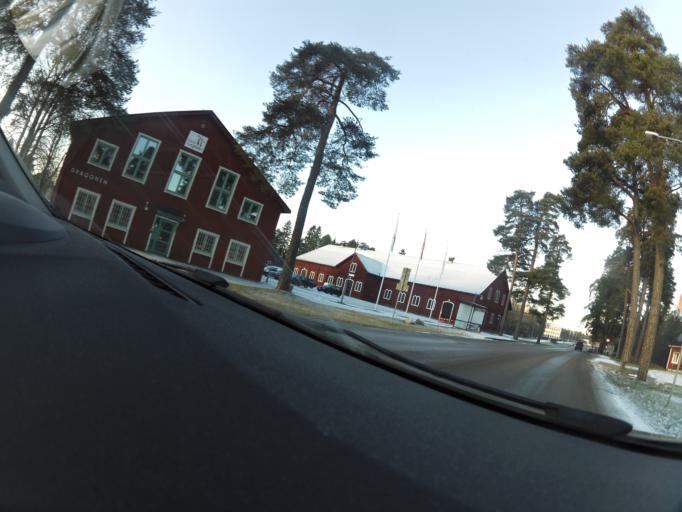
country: SE
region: Gaevleborg
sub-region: Gavle Kommun
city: Gavle
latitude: 60.6681
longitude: 17.1104
